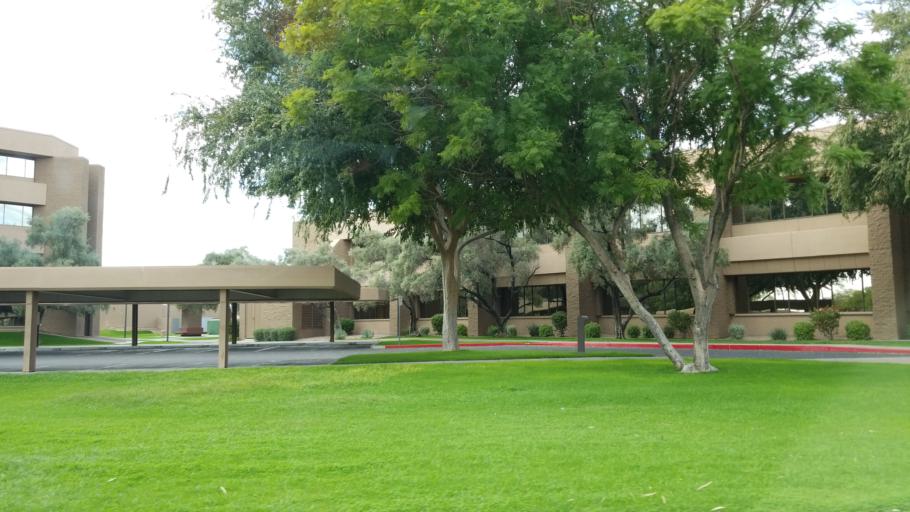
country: US
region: Arizona
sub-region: Maricopa County
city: Glendale
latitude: 33.5777
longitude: -112.1144
